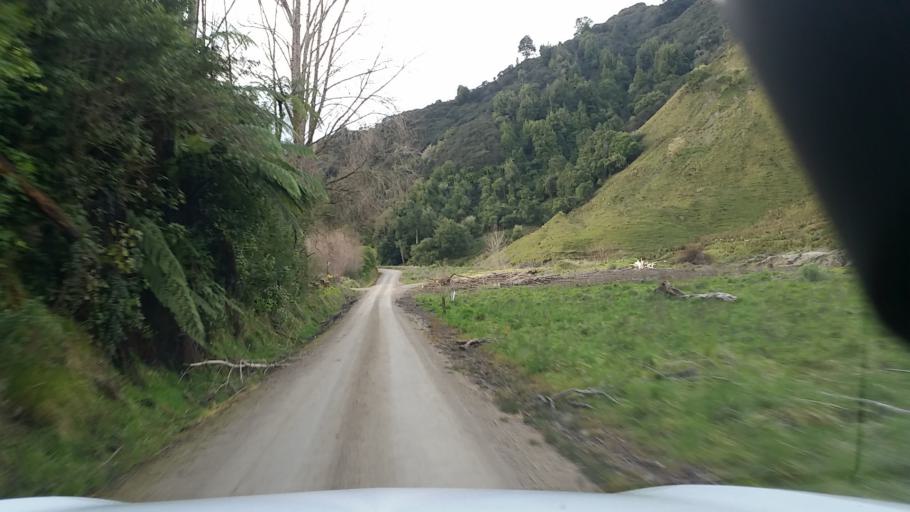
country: NZ
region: Taranaki
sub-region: South Taranaki District
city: Patea
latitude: -39.5690
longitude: 174.8099
